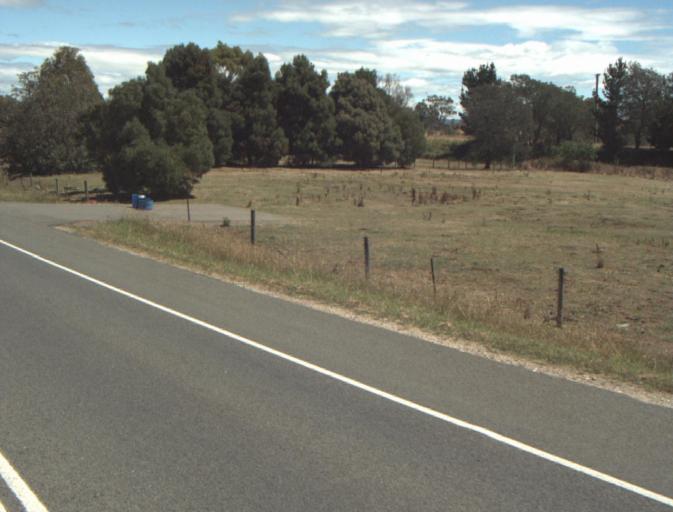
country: AU
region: Tasmania
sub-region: Launceston
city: Mayfield
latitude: -41.3710
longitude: 147.1391
